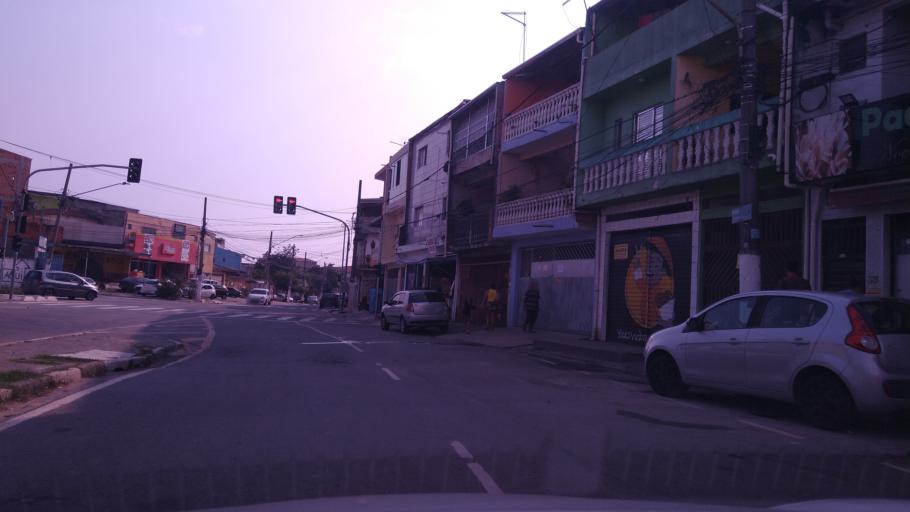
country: BR
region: Sao Paulo
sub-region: Osasco
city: Osasco
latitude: -23.5123
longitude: -46.7818
